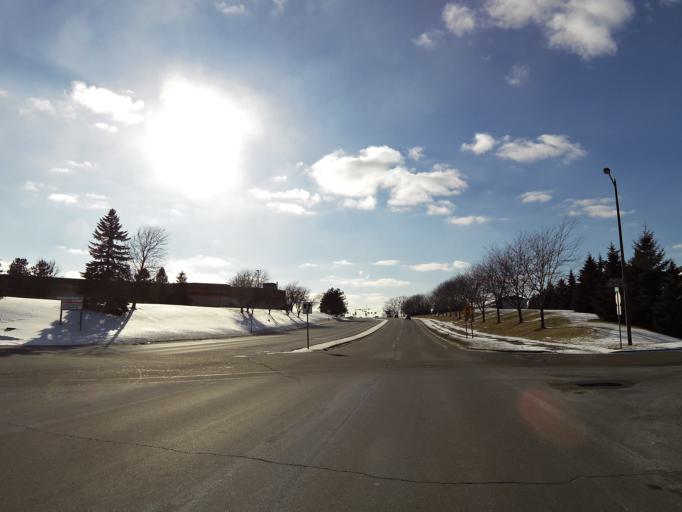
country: US
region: Minnesota
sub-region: Dakota County
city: Burnsville
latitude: 44.7491
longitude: -93.2987
